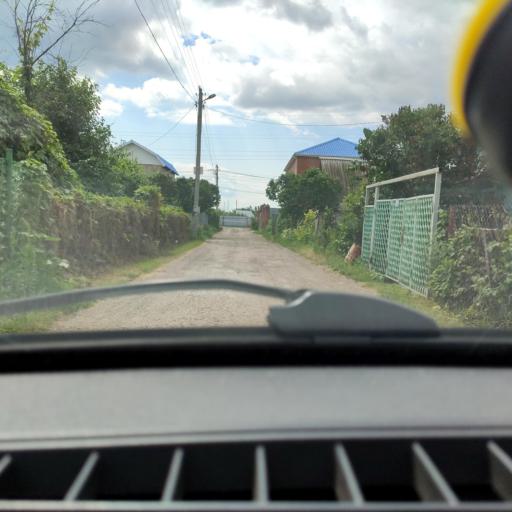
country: RU
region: Samara
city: Podstepki
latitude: 53.5980
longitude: 49.2245
